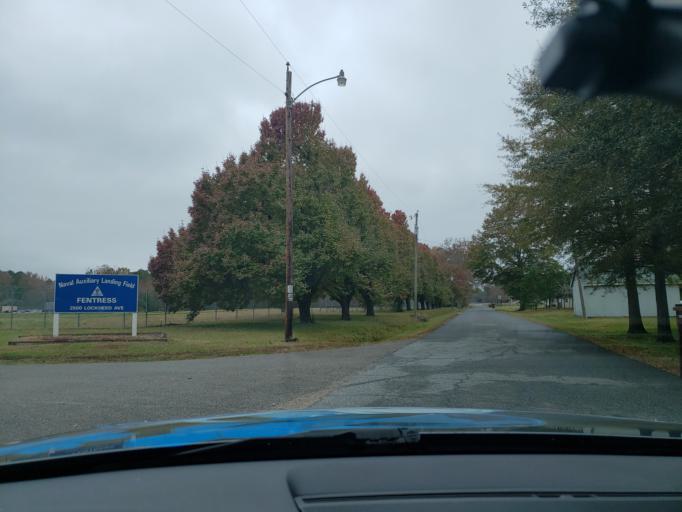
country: US
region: Virginia
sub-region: City of Chesapeake
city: Chesapeake
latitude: 36.7081
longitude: -76.1279
